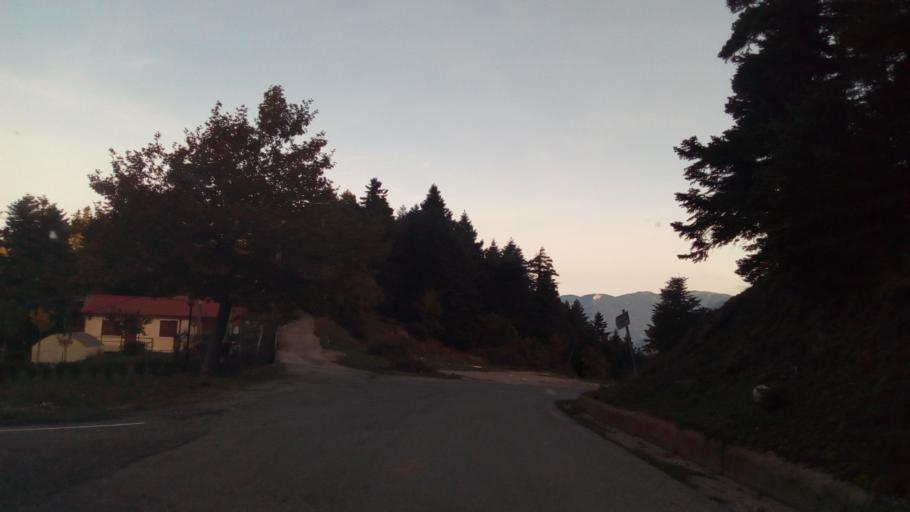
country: GR
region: West Greece
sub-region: Nomos Aitolias kai Akarnanias
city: Thermo
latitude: 38.6359
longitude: 21.8355
